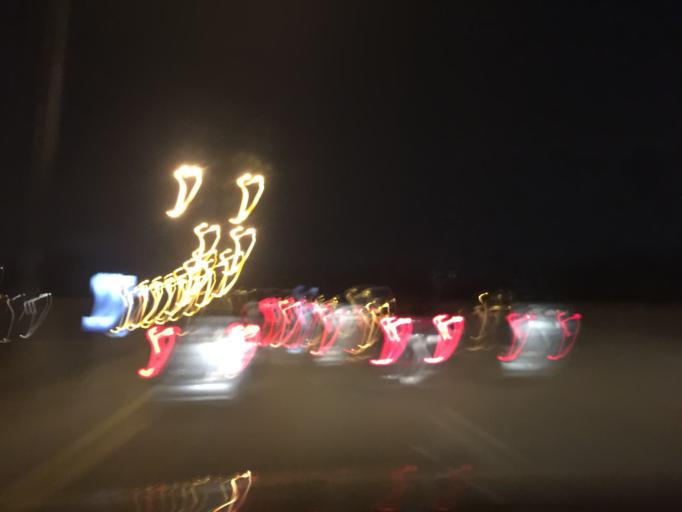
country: JO
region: Amman
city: Umm as Summaq
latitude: 31.9267
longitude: 35.8600
